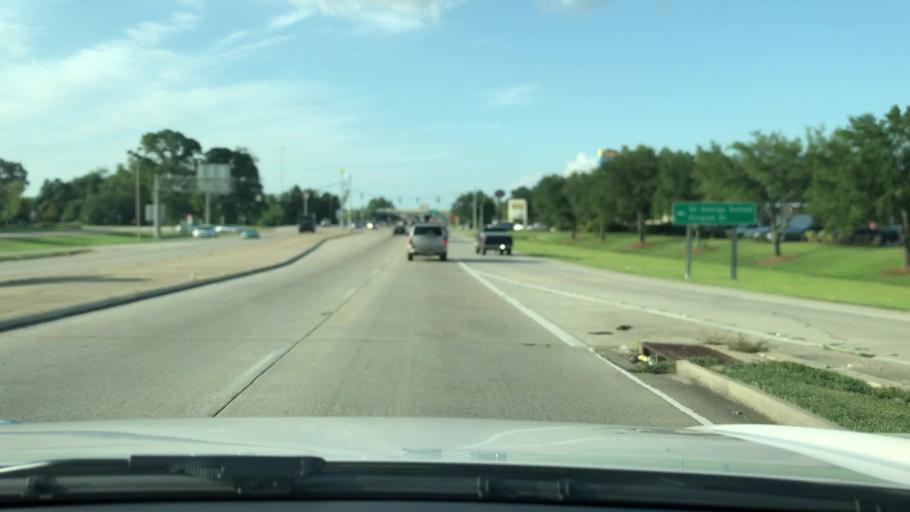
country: US
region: Louisiana
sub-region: East Baton Rouge Parish
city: Village Saint George
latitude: 30.3781
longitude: -91.0679
